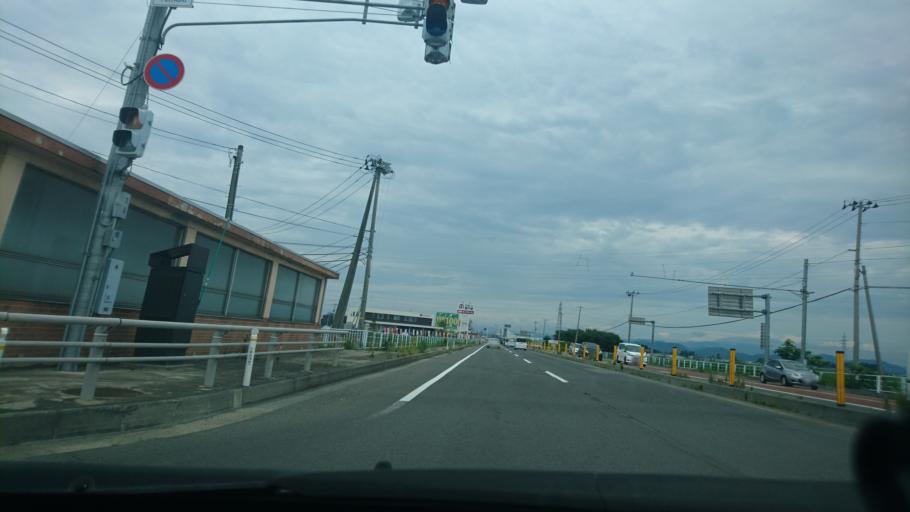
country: JP
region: Akita
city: Omagari
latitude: 39.4510
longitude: 140.5003
